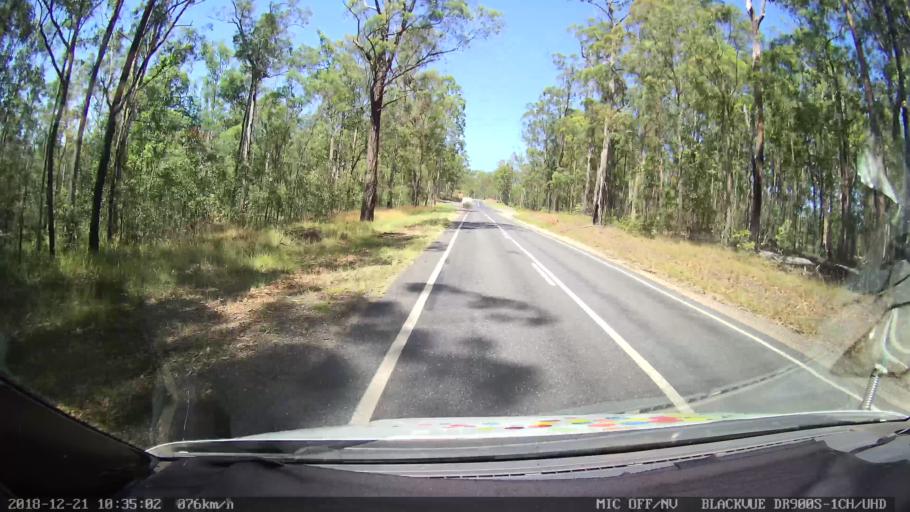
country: AU
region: New South Wales
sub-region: Clarence Valley
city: South Grafton
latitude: -29.6170
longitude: 152.6482
